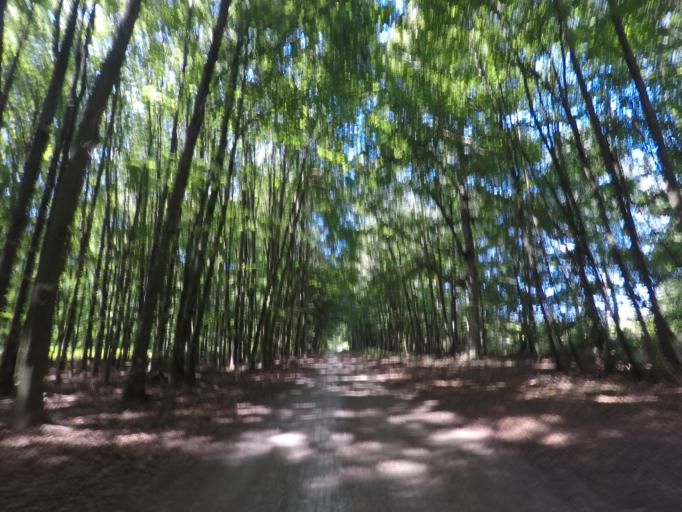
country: LU
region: Luxembourg
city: Bridel
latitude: 49.6459
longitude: 6.0886
